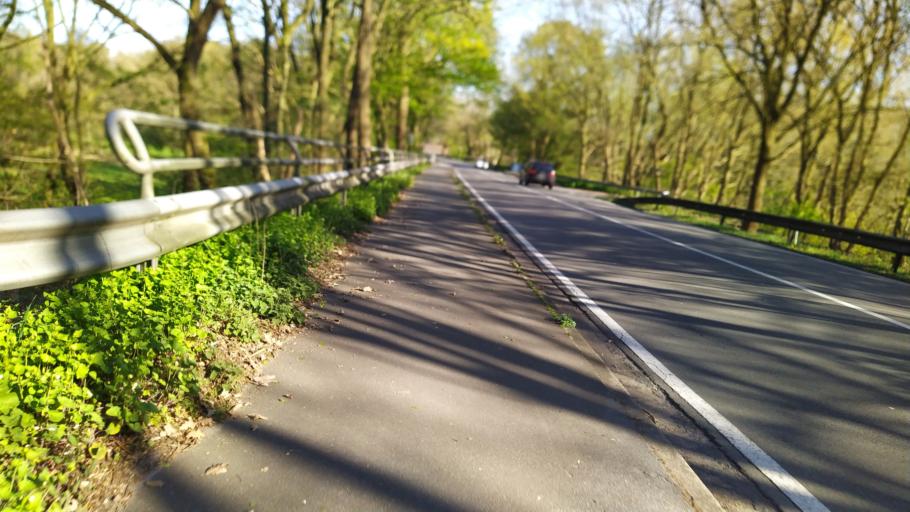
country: DE
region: Lower Saxony
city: Hamersen
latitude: 53.2813
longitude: 9.4766
